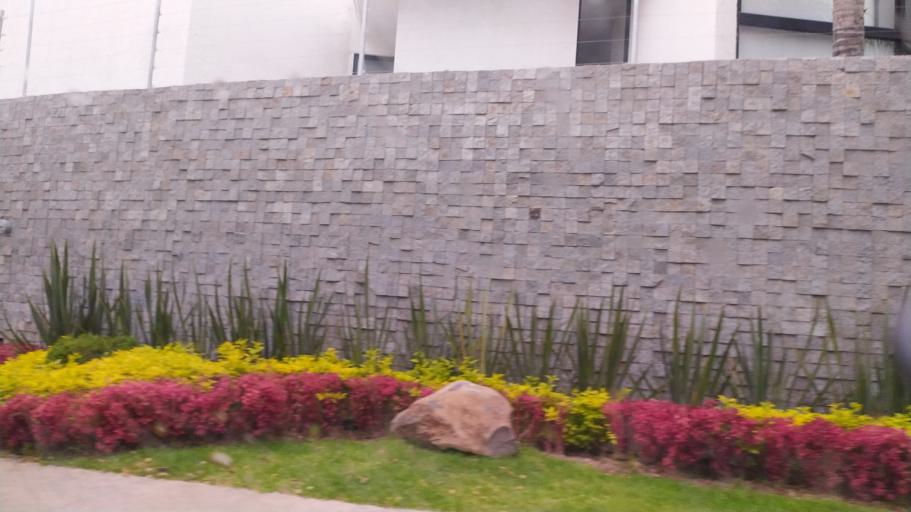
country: MX
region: Jalisco
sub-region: Zapopan
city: Zapopan
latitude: 20.7186
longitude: -103.3816
